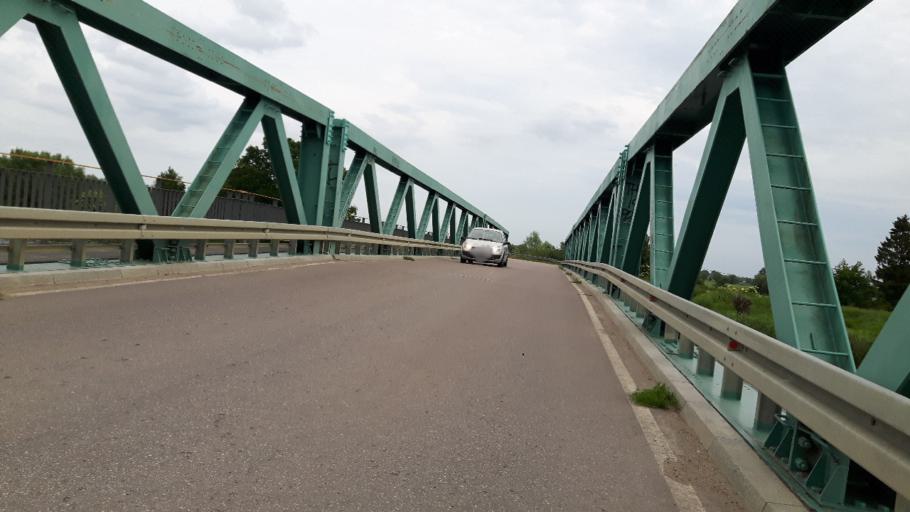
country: PL
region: Warmian-Masurian Voivodeship
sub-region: Powiat elblaski
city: Elblag
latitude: 54.1892
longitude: 19.3145
